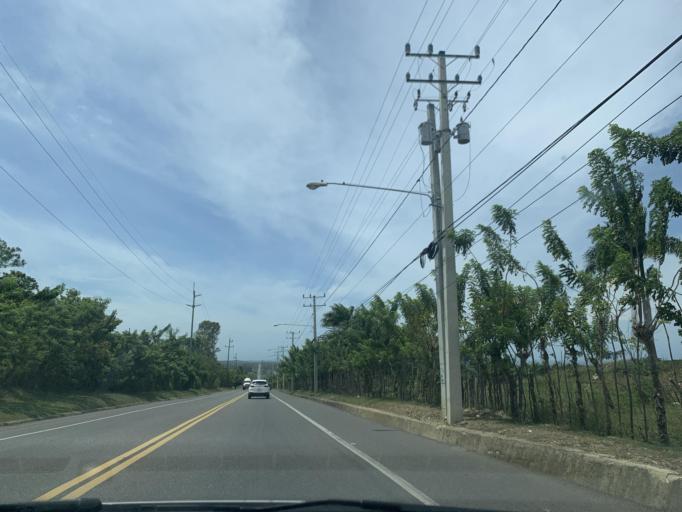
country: DO
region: Puerto Plata
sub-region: Puerto Plata
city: Puerto Plata
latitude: 19.7309
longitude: -70.6266
